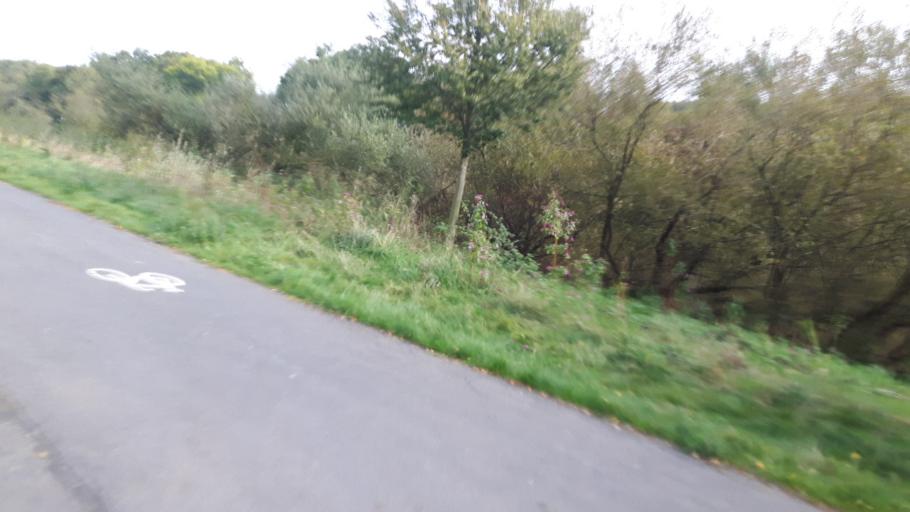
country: DE
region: North Rhine-Westphalia
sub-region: Regierungsbezirk Koln
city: Eitorf
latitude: 50.7754
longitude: 7.4135
